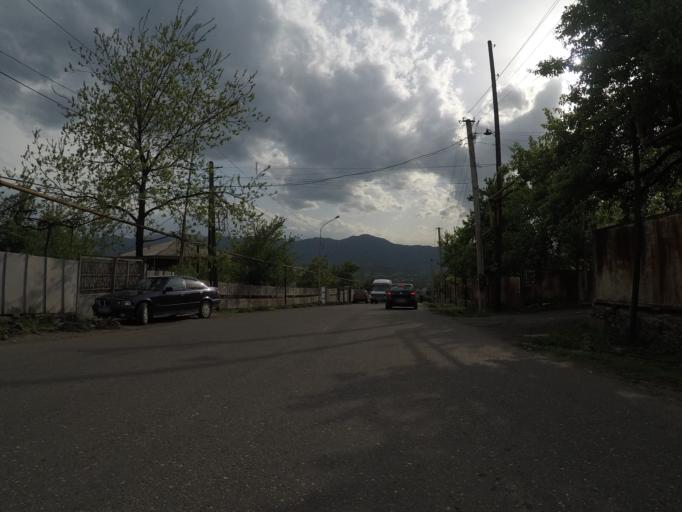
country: GE
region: Imereti
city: Zestap'oni
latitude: 42.1147
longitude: 43.0495
